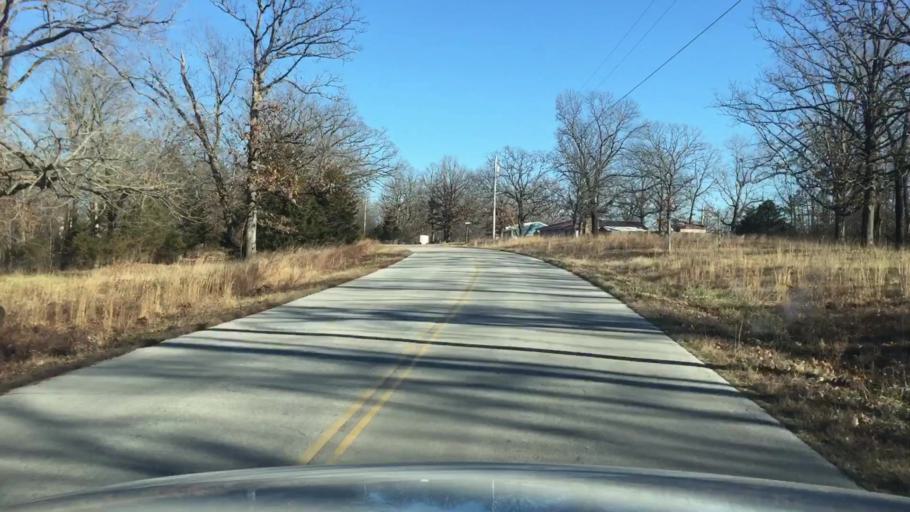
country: US
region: Missouri
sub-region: Morgan County
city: Versailles
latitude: 38.3357
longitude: -92.7649
